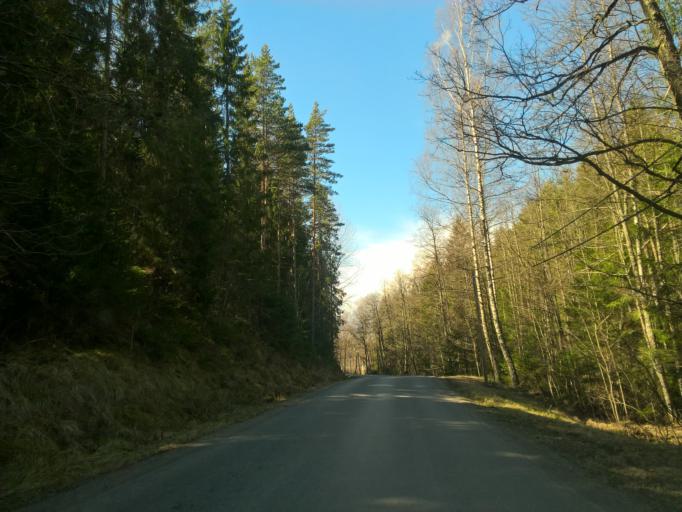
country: SE
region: OEstergoetland
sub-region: Finspangs Kommun
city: Finspang
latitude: 58.7288
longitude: 15.7540
